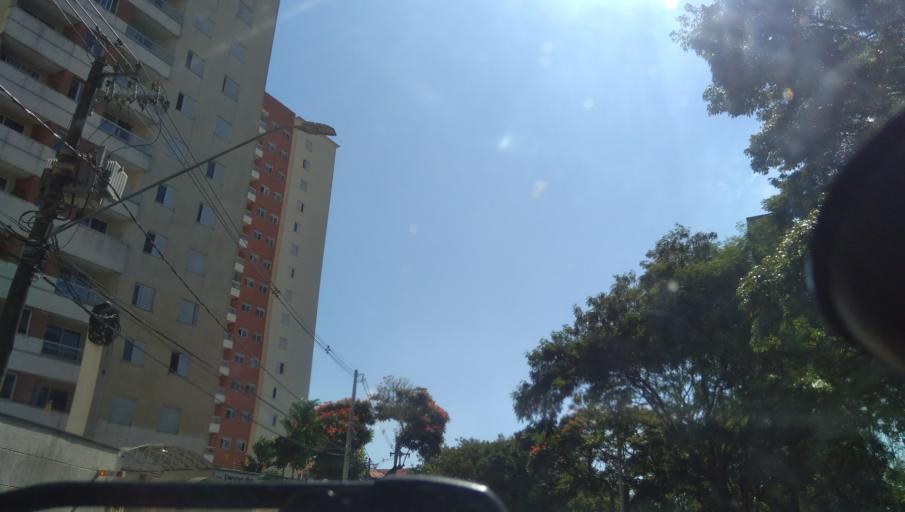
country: BR
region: Sao Paulo
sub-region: Sao Jose Dos Campos
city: Sao Jose dos Campos
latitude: -23.1653
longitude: -45.8926
